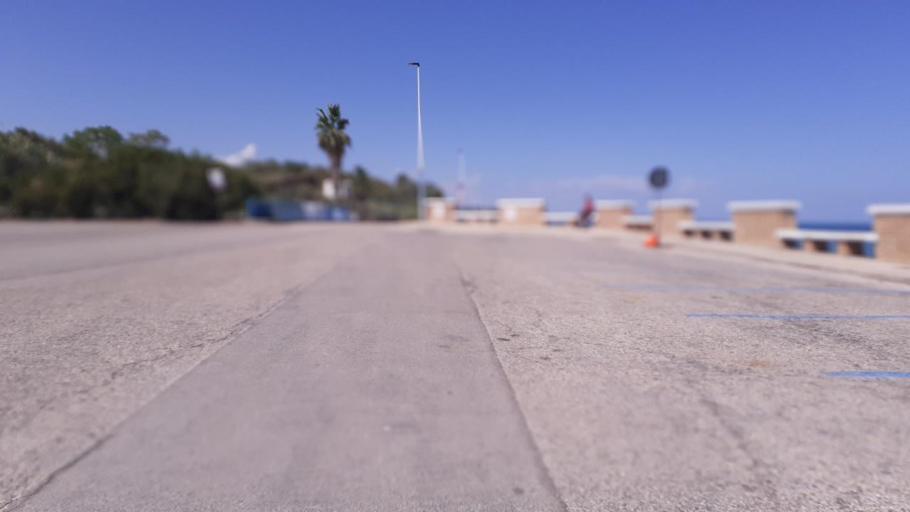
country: IT
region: Abruzzo
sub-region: Provincia di Chieti
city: Casalbordino-Miracoli
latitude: 42.1961
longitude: 14.6289
